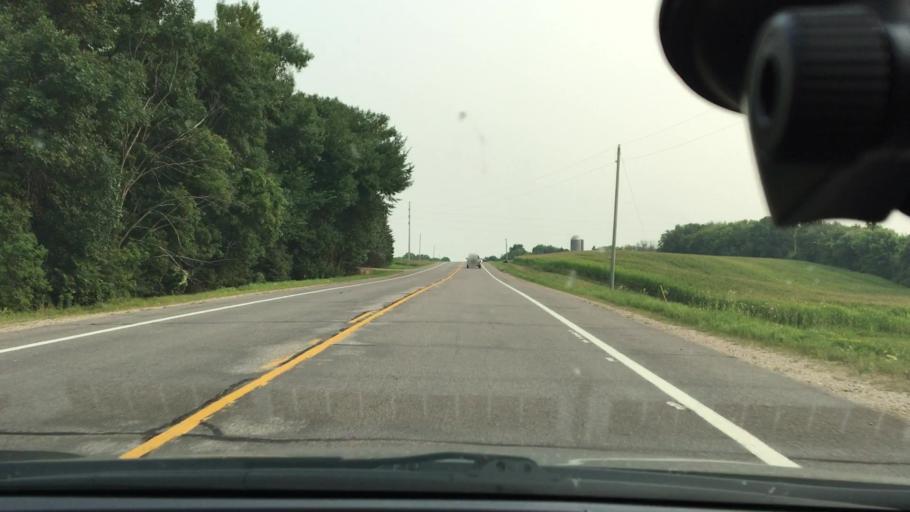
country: US
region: Minnesota
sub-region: Wright County
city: Albertville
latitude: 45.2831
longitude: -93.6637
